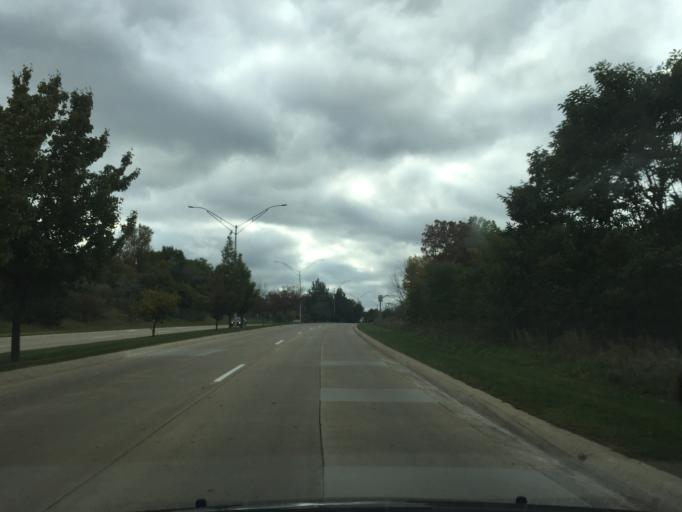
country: US
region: Michigan
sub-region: Oakland County
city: Auburn Hills
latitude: 42.6599
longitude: -83.2174
